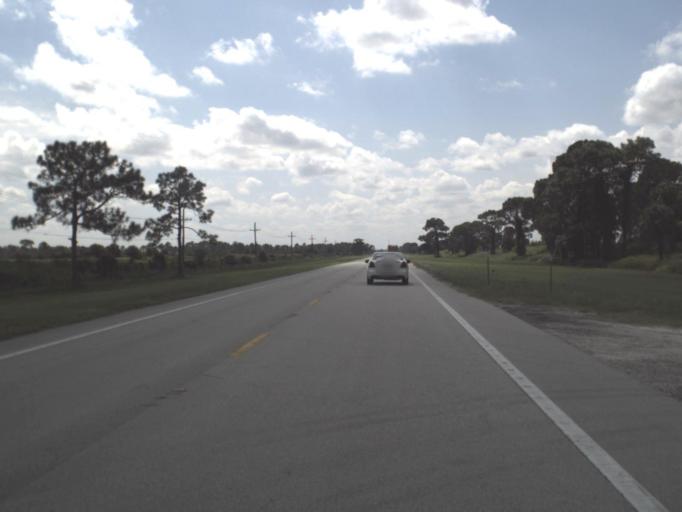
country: US
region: Florida
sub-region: Hendry County
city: Port LaBelle
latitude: 26.6181
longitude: -81.4365
